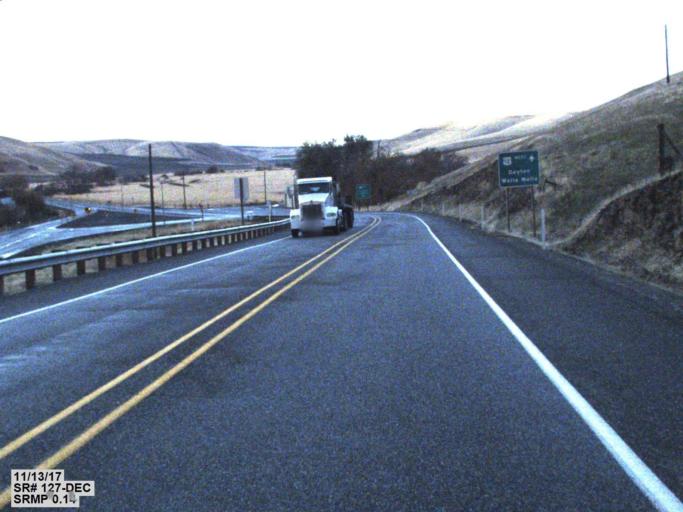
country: US
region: Washington
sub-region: Garfield County
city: Pomeroy
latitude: 46.5242
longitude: -117.8197
